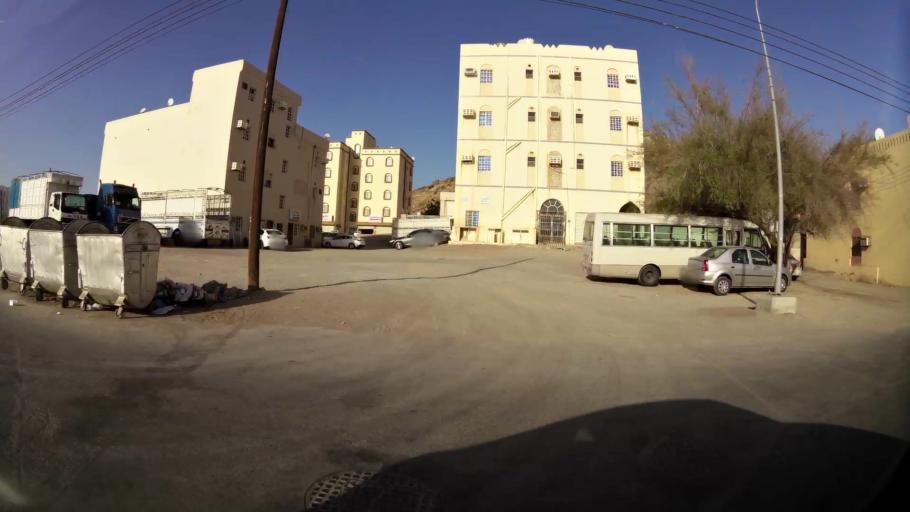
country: OM
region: Muhafazat Masqat
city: Muscat
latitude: 23.5849
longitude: 58.5513
